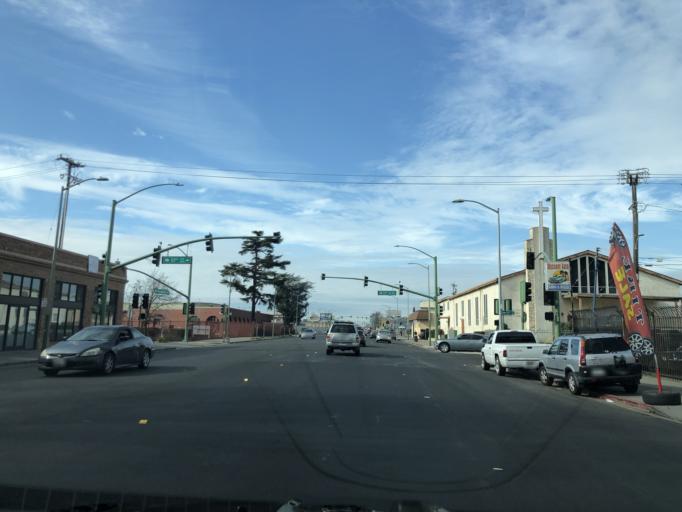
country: US
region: California
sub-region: Alameda County
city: Alameda
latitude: 37.7659
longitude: -122.2011
